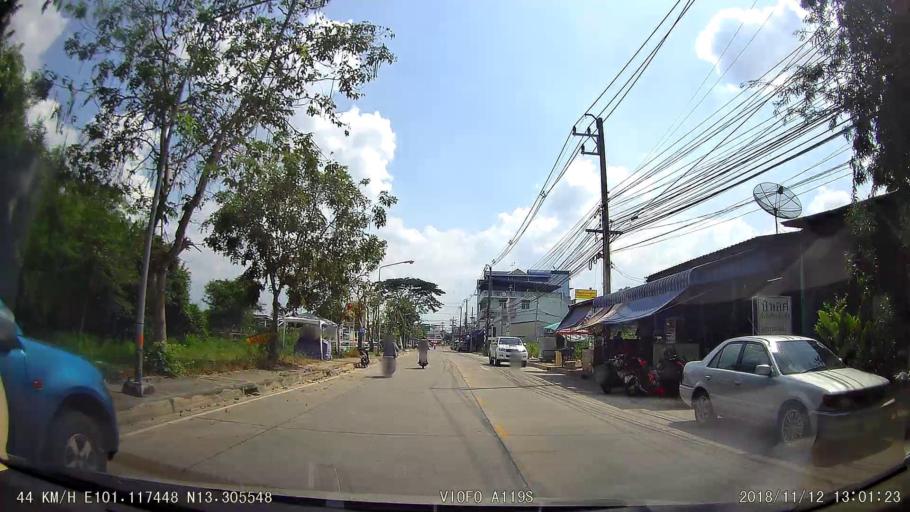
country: TH
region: Chon Buri
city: Ban Bueng
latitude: 13.3053
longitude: 101.1176
